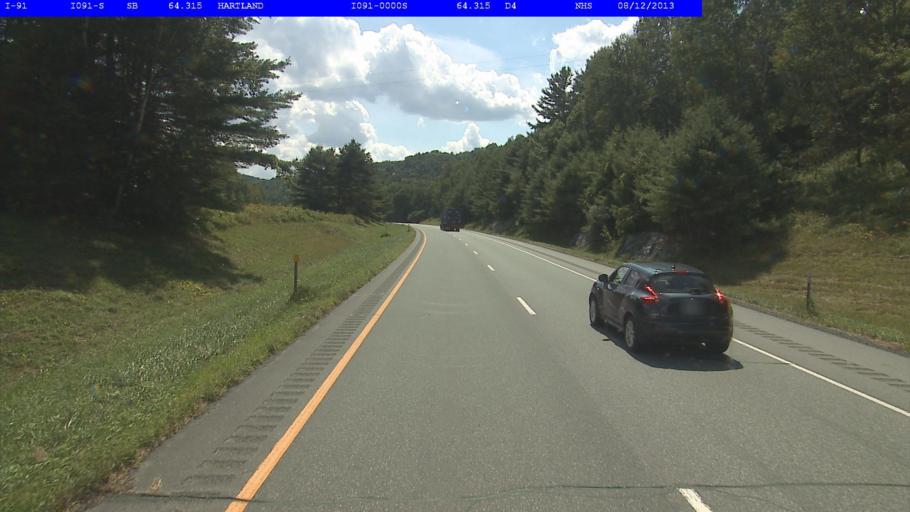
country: US
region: Vermont
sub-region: Windsor County
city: White River Junction
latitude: 43.5792
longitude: -72.3829
